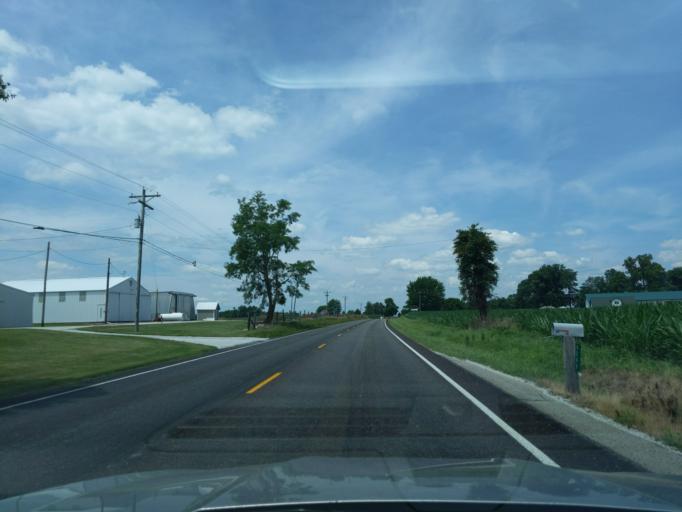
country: US
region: Indiana
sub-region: Ripley County
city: Osgood
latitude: 39.2103
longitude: -85.3316
